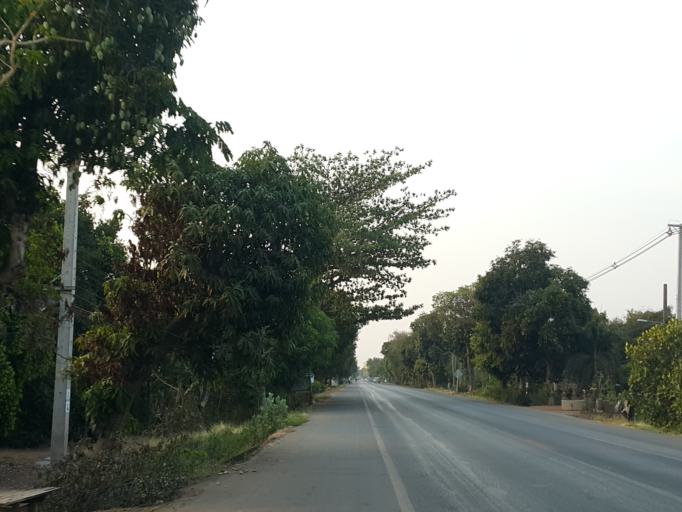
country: TH
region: Sukhothai
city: Si Samrong
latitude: 17.2311
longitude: 99.8582
